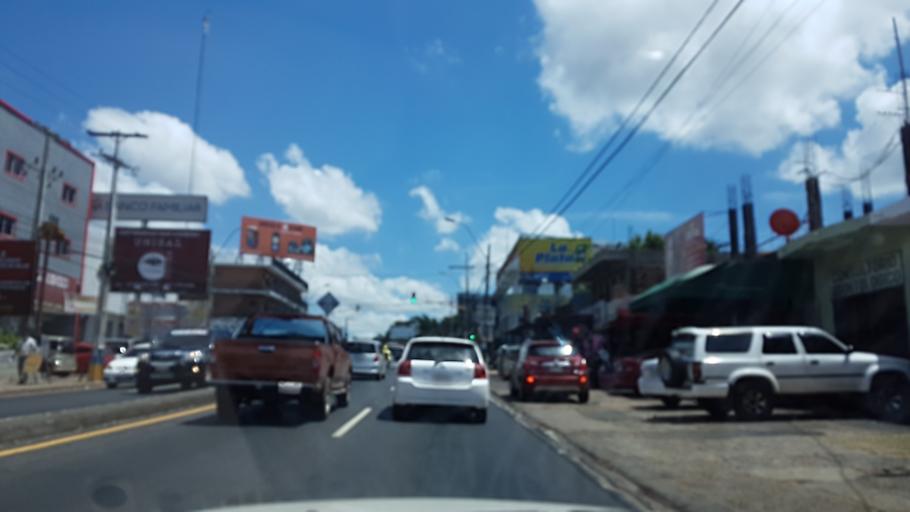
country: PY
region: Central
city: Capiata
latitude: -25.3536
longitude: -57.4432
